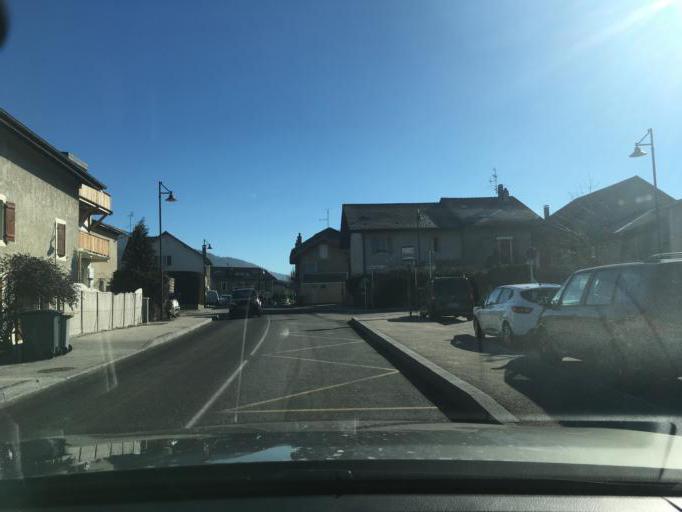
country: FR
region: Rhone-Alpes
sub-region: Departement de la Haute-Savoie
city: Cranves-Sales
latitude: 46.1798
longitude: 6.2999
